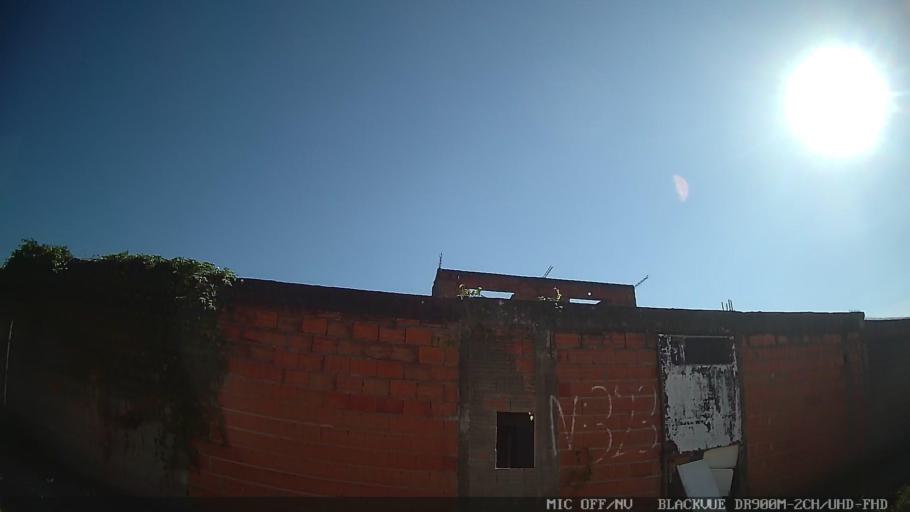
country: BR
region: Sao Paulo
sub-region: Guaruja
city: Guaruja
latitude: -23.9716
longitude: -46.2122
